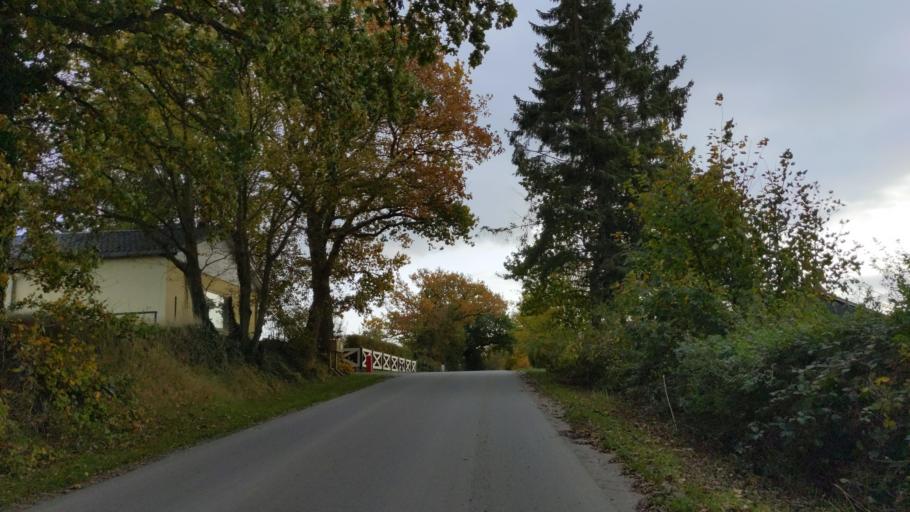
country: DE
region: Schleswig-Holstein
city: Kasseedorf
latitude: 54.1285
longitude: 10.7051
